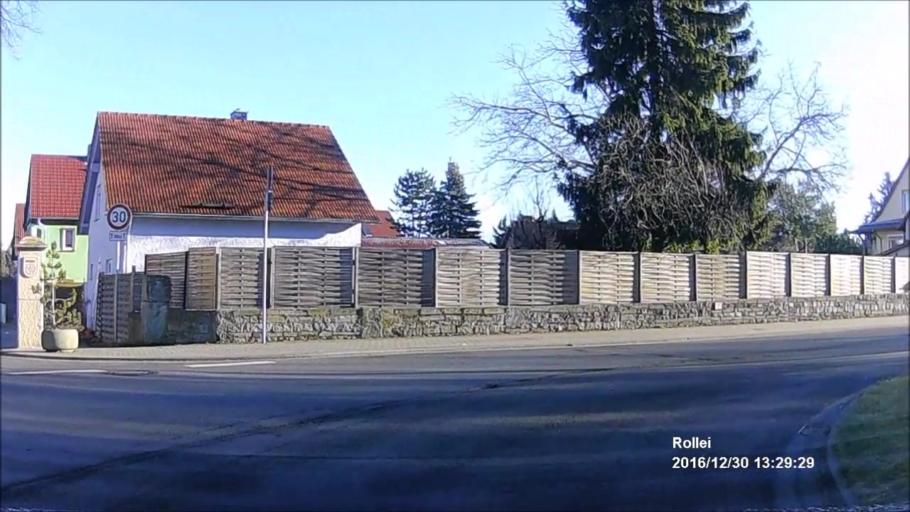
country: DE
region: Thuringia
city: Monchenholzhausen
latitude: 50.9470
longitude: 11.0914
